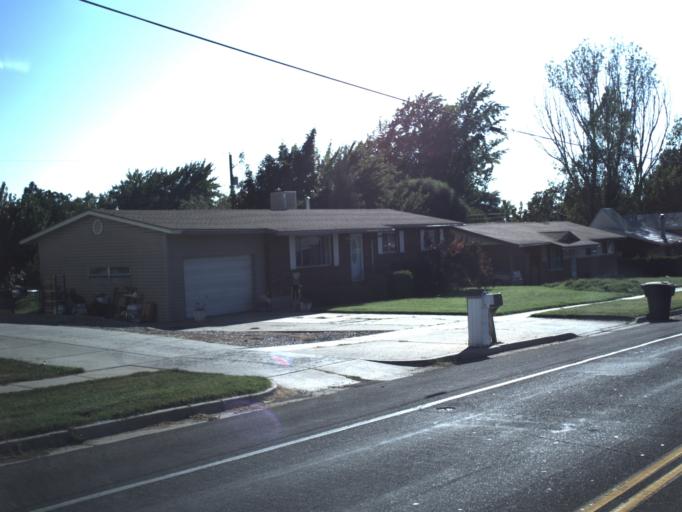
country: US
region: Utah
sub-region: Davis County
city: Sunset
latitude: 41.1399
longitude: -112.0370
